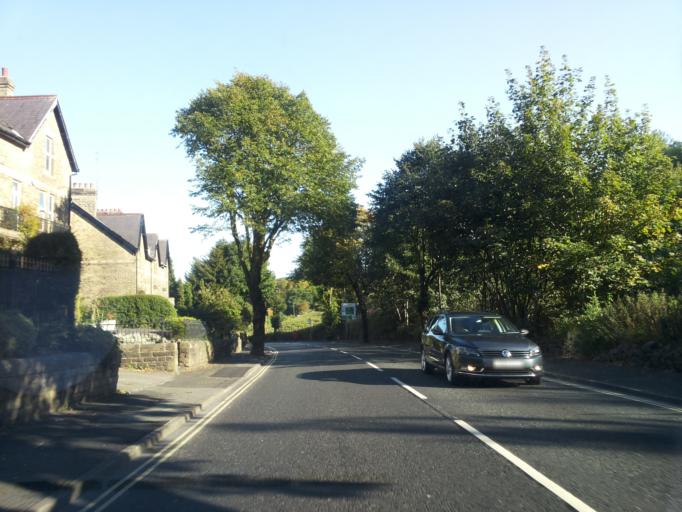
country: GB
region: England
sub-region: Derbyshire
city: Buxton
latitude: 53.2542
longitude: -1.9074
